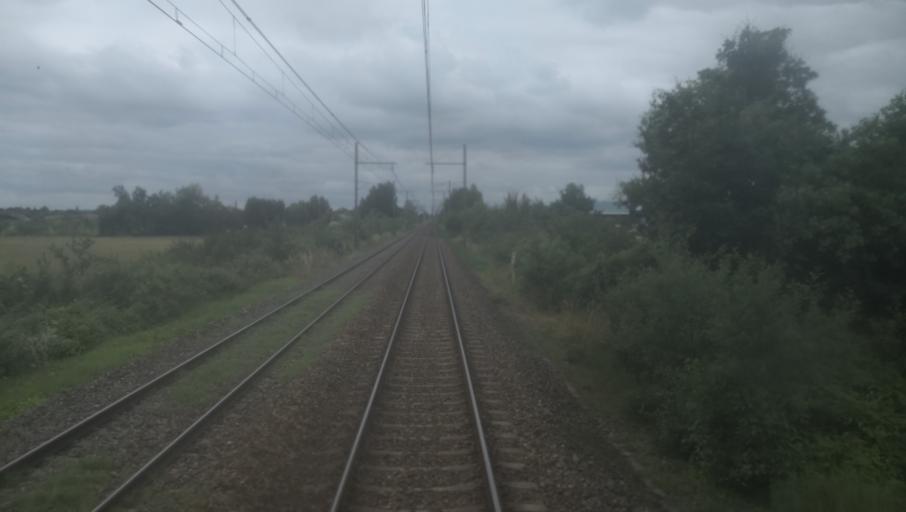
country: FR
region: Midi-Pyrenees
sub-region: Departement du Tarn-et-Garonne
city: Montauban
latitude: 44.0169
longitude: 1.3269
